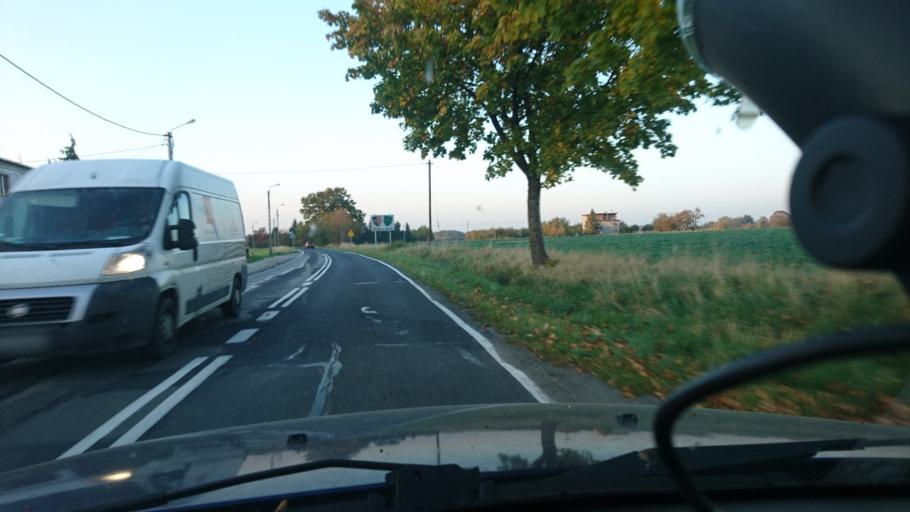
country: PL
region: Silesian Voivodeship
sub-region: Powiat bielski
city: Kozy
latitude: 49.8464
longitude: 19.1170
